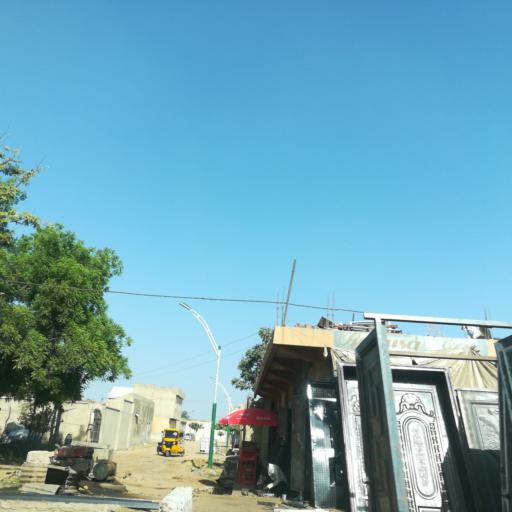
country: NG
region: Kano
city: Kano
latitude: 12.0216
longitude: 8.5029
